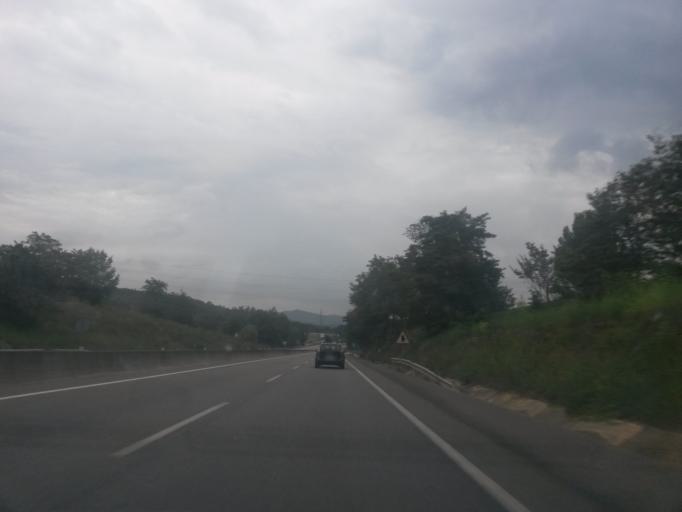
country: ES
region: Catalonia
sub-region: Provincia de Girona
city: Palol de Revardit
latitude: 42.0576
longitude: 2.8148
